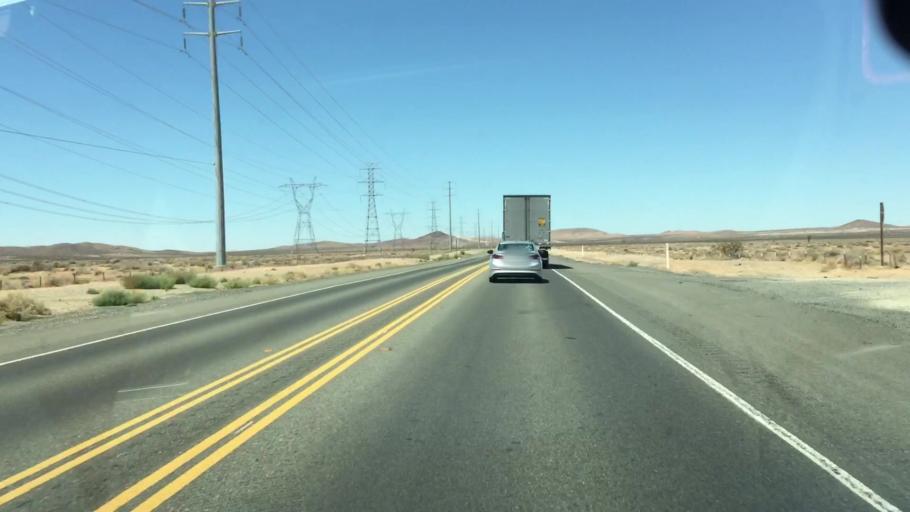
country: US
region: California
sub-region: Kern County
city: Boron
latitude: 34.8211
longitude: -117.4941
